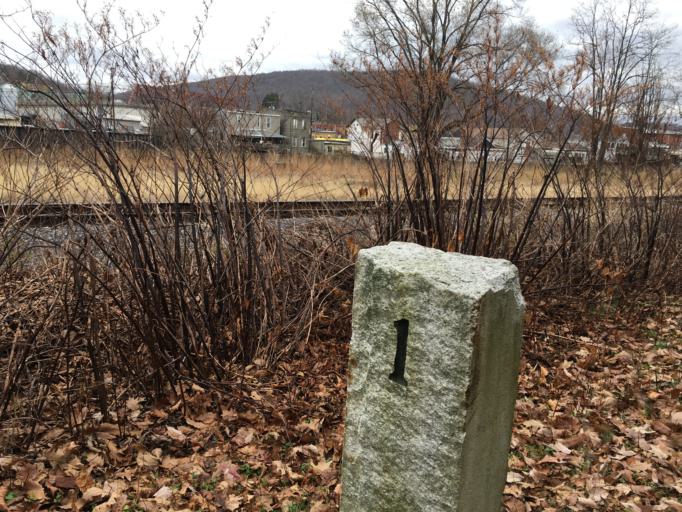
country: US
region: Maryland
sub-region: Allegany County
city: Cumberland
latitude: 39.6585
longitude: -78.7761
